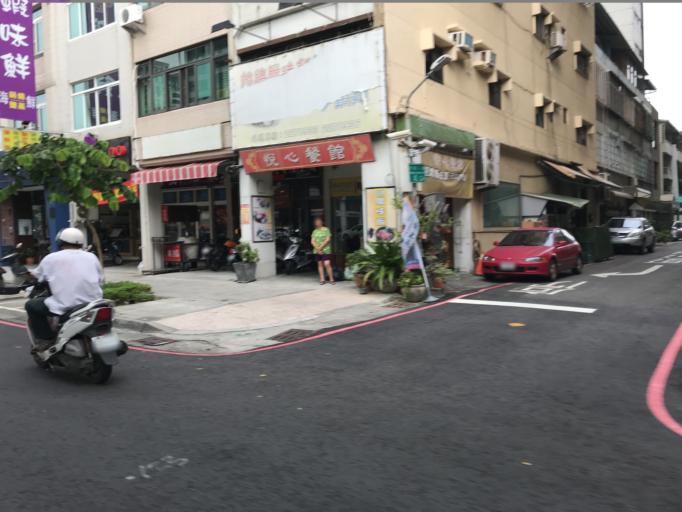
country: TW
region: Kaohsiung
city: Kaohsiung
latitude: 22.6314
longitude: 120.3136
